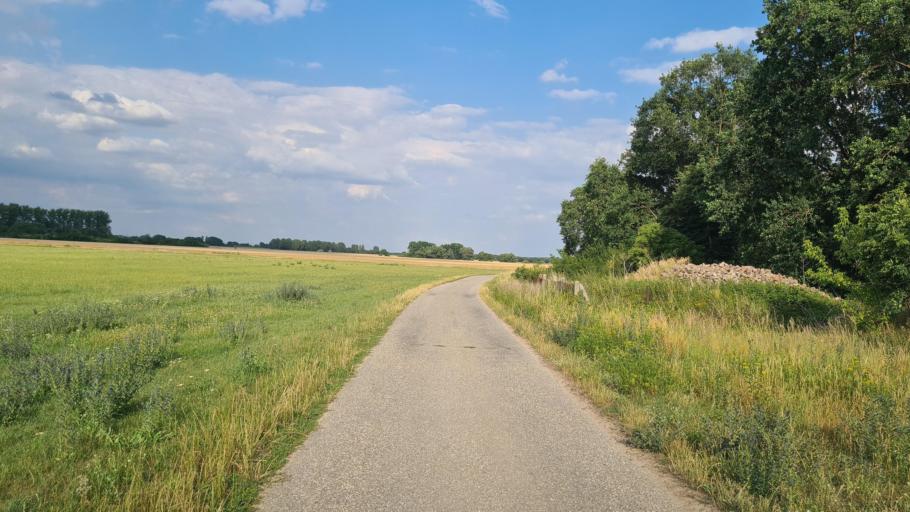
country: DE
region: Saxony-Anhalt
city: Pretzsch
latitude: 51.7636
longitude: 12.8433
